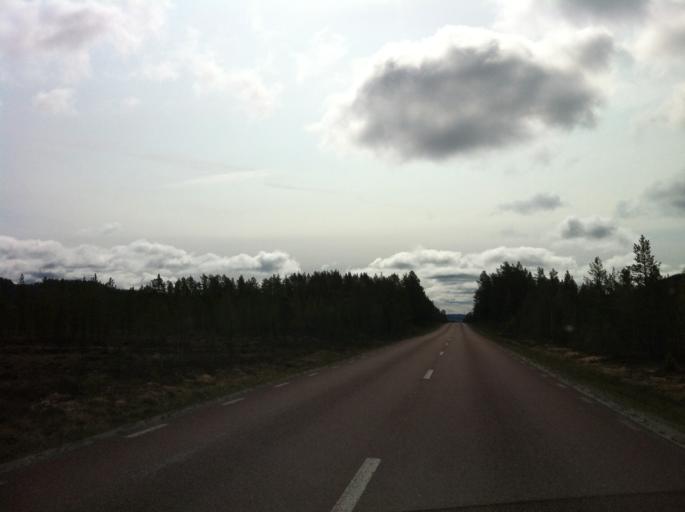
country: NO
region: Hedmark
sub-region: Engerdal
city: Engerdal
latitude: 62.4894
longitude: 12.6454
